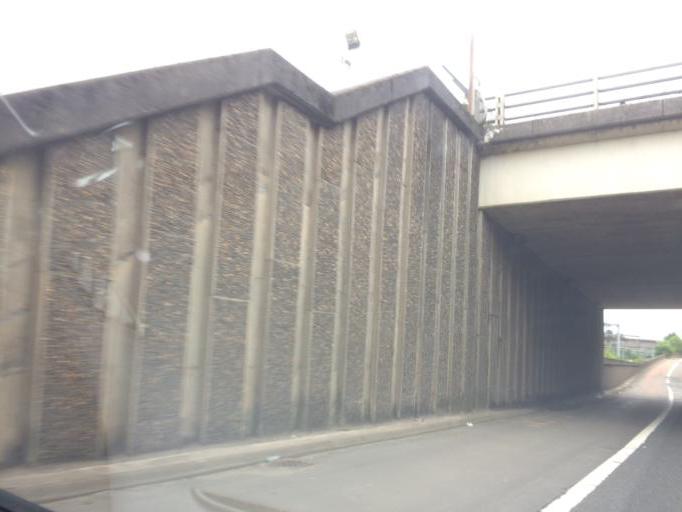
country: GB
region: Scotland
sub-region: Renfrewshire
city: Renfrew
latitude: 55.8529
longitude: -4.3403
